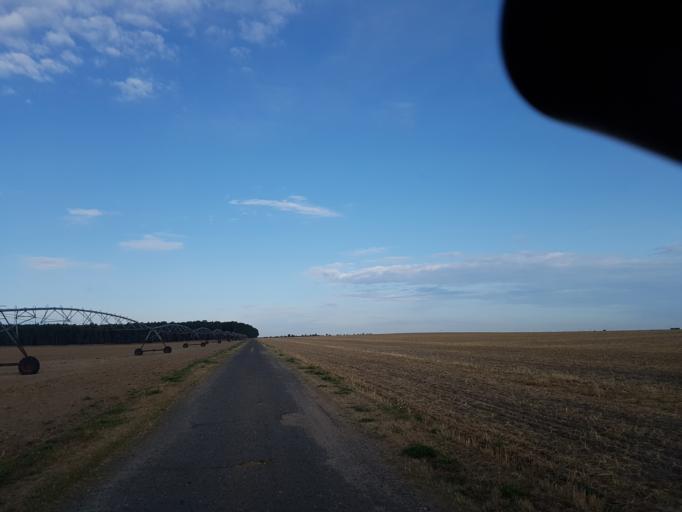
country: DE
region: Brandenburg
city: Niedergorsdorf
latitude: 51.9334
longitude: 13.0171
